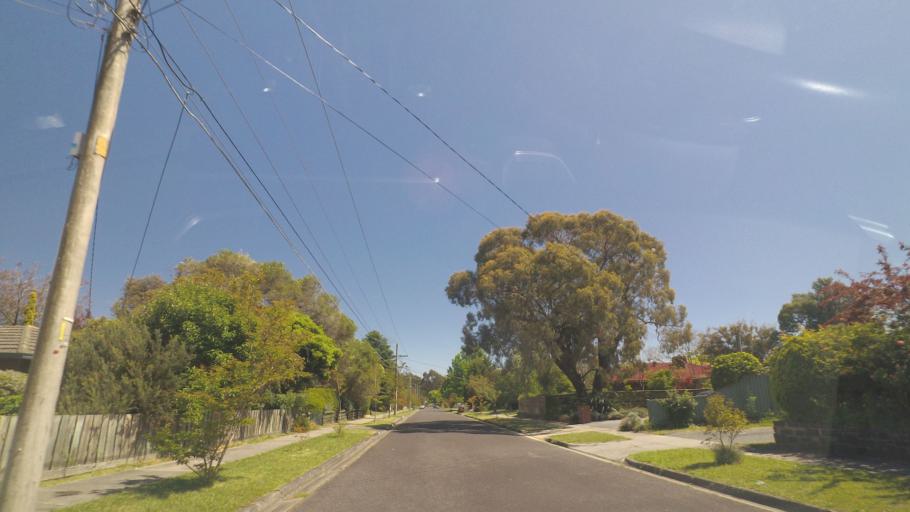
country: AU
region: Victoria
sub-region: Maroondah
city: Croydon Hills
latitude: -37.7871
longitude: 145.2648
